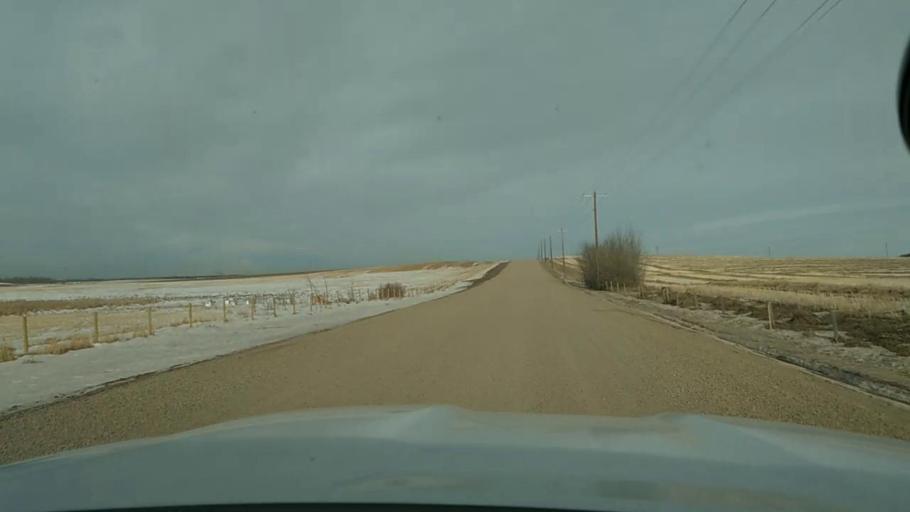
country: CA
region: Alberta
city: Airdrie
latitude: 51.2370
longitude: -113.9118
